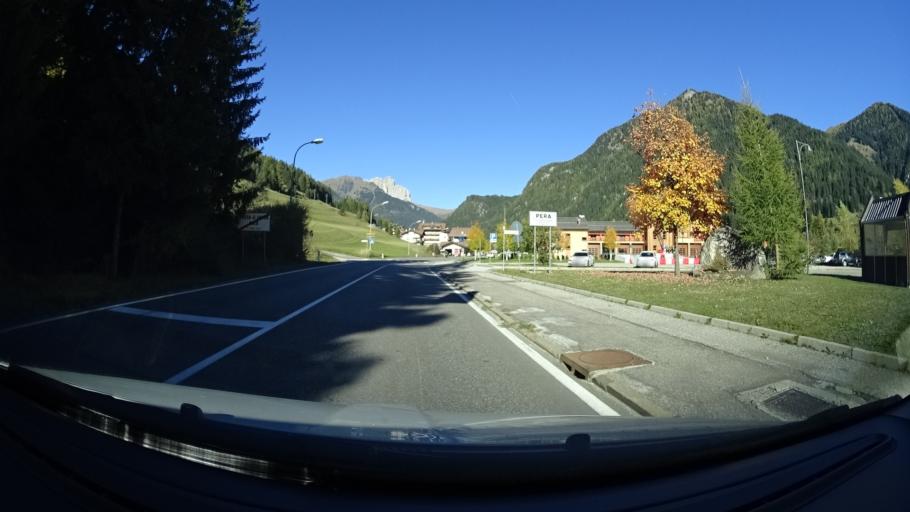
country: IT
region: Trentino-Alto Adige
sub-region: Provincia di Trento
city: Pozza di Fassa
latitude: 46.4328
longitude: 11.6872
